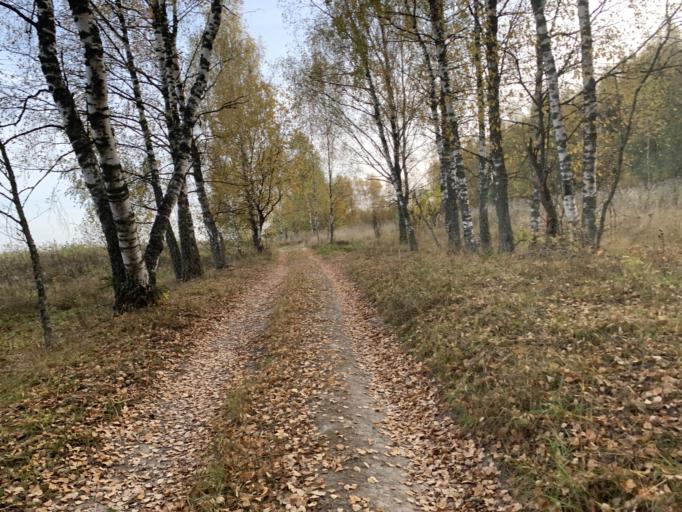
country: RU
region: Jaroslavl
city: Porech'ye-Rybnoye
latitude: 56.9848
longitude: 39.3803
